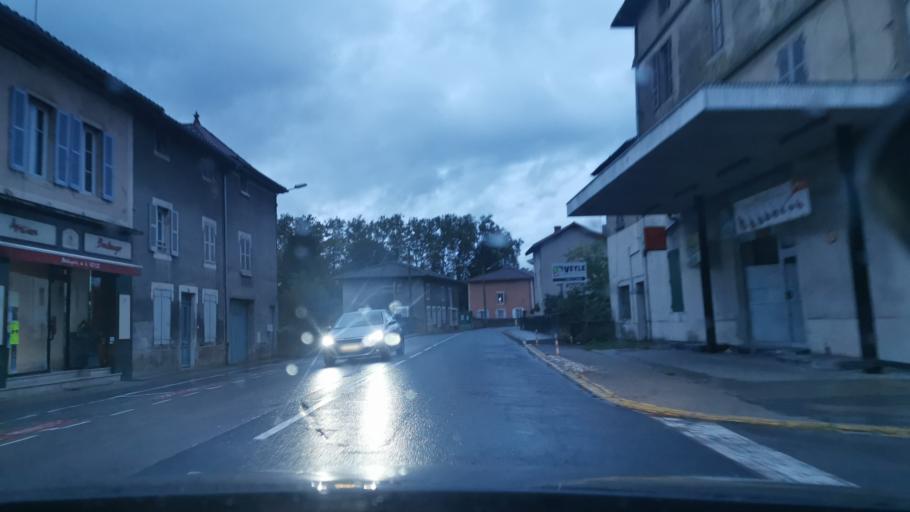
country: FR
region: Rhone-Alpes
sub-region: Departement de l'Ain
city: Pont-de-Veyle
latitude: 46.2656
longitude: 4.8893
